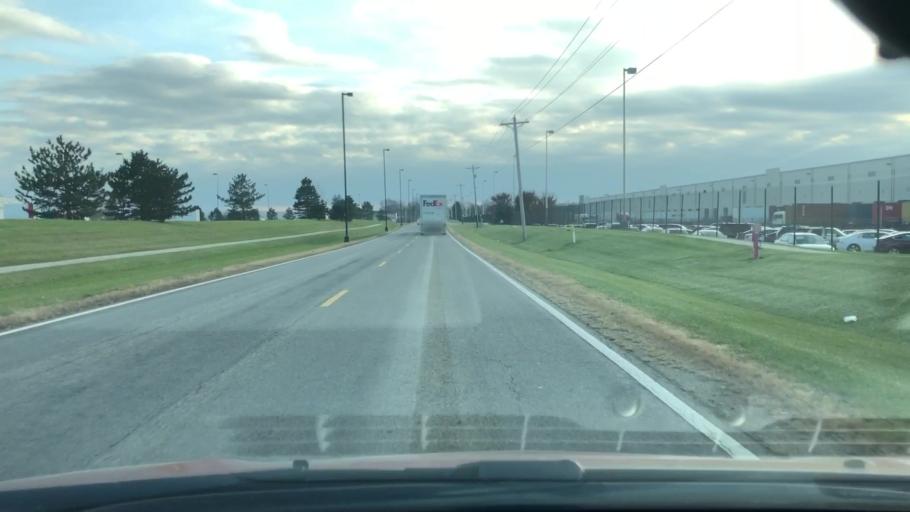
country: US
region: Ohio
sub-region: Franklin County
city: Obetz
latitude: 39.8349
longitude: -82.9442
